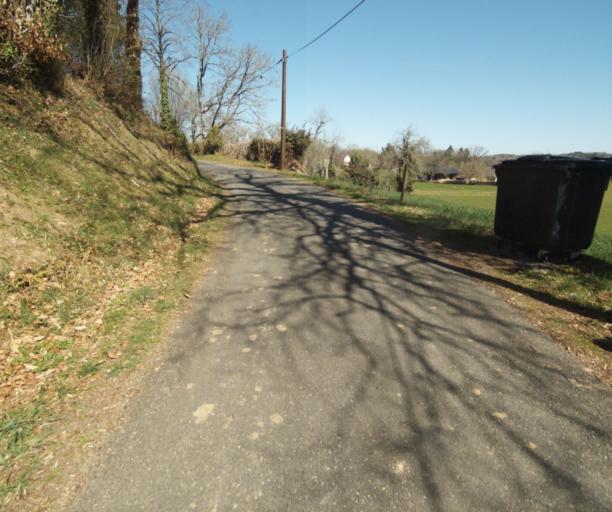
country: FR
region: Limousin
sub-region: Departement de la Correze
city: Saint-Mexant
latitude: 45.3024
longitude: 1.6469
